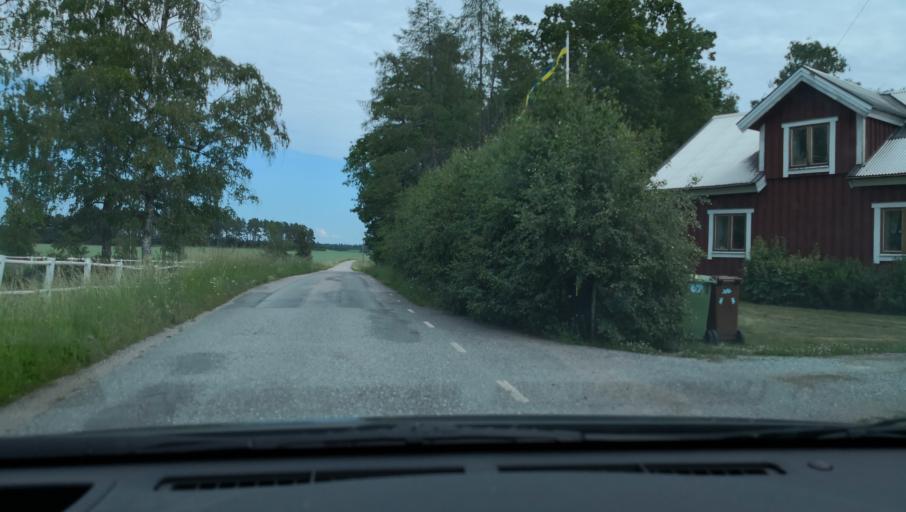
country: SE
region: Uppsala
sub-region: Enkopings Kommun
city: Orsundsbro
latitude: 59.6928
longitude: 17.3919
